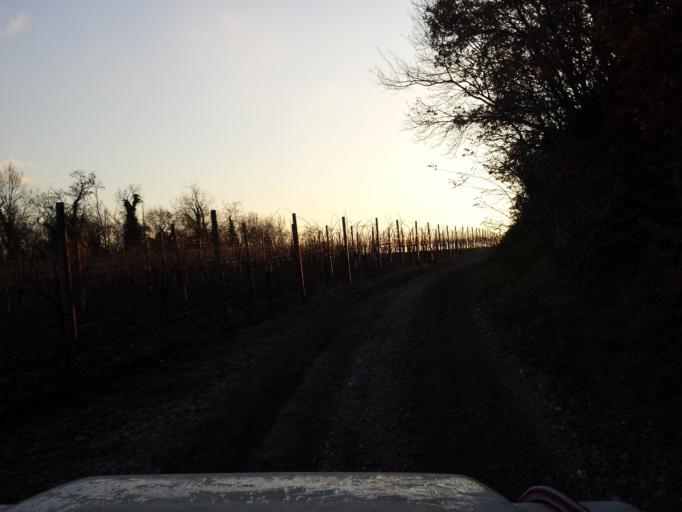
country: IT
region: Friuli Venezia Giulia
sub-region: Provincia di Gorizia
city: Dolegna del Collio
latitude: 46.0191
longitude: 13.4879
